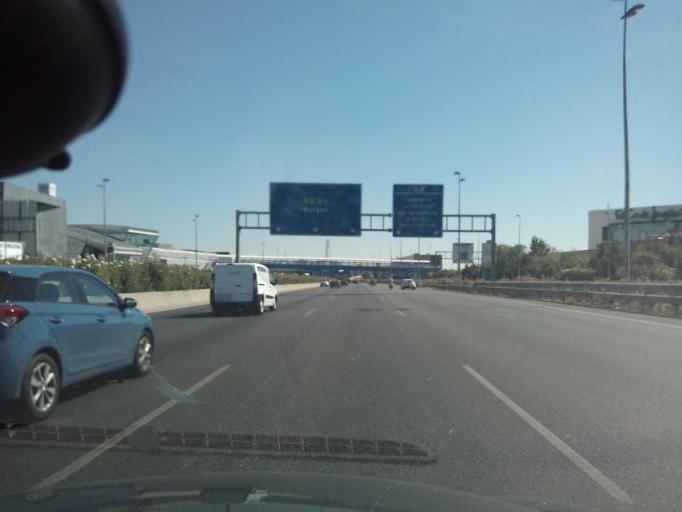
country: ES
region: Madrid
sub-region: Provincia de Madrid
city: Las Tablas
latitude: 40.4967
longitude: -3.6650
